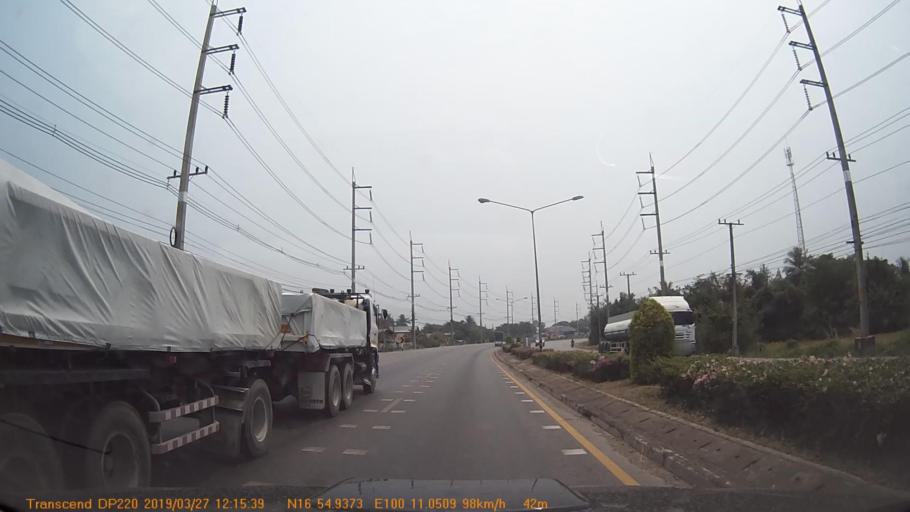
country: TH
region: Phitsanulok
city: Phitsanulok
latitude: 16.9155
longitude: 100.1844
